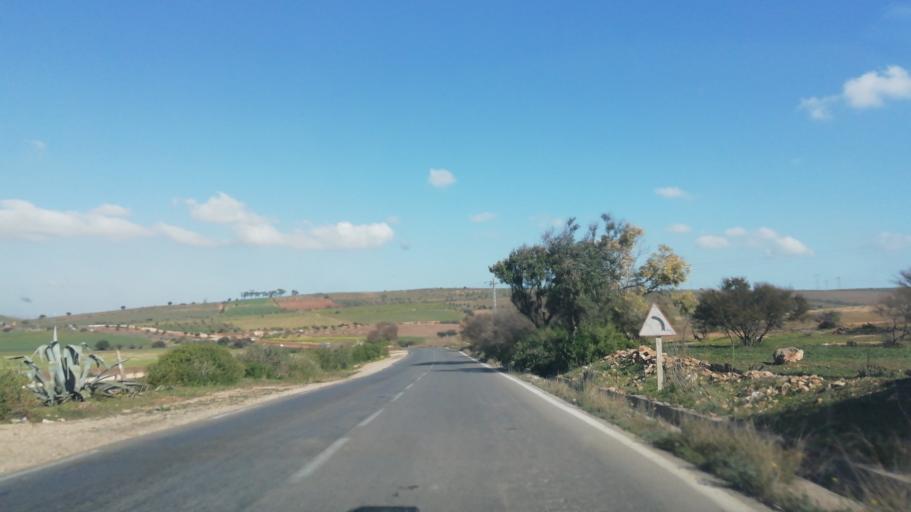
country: DZ
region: Oran
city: Ain el Bya
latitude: 35.7333
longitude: -0.2527
